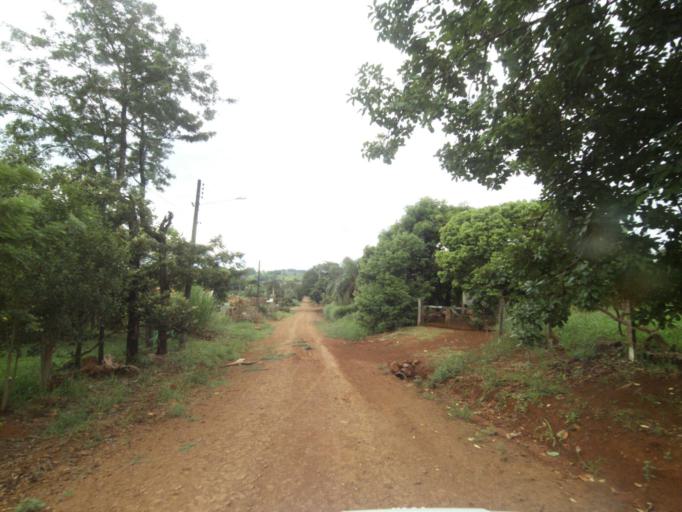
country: BR
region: Parana
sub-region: Guaraniacu
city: Guaraniacu
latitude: -24.9221
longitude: -52.9397
